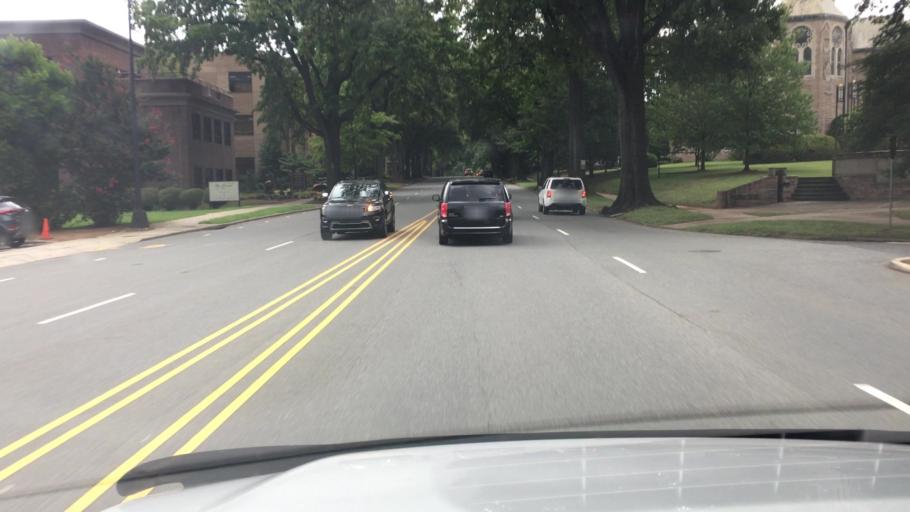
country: US
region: North Carolina
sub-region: Mecklenburg County
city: Charlotte
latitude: 35.2132
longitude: -80.8440
